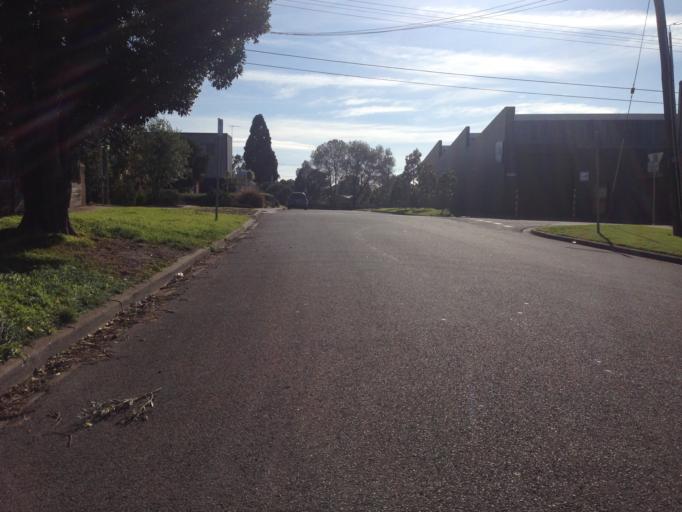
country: AU
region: Victoria
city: Heidelberg West
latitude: -37.7602
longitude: 145.0255
